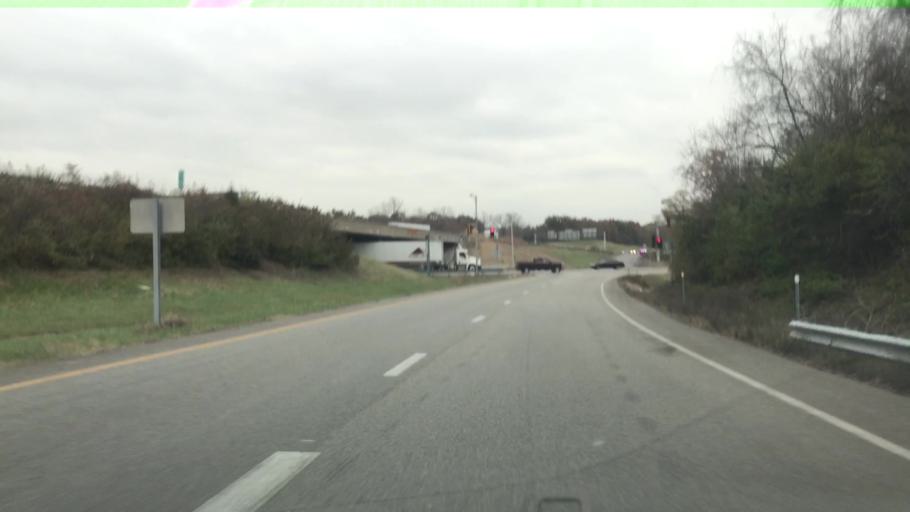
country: US
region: Missouri
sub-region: Clay County
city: Claycomo
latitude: 39.2033
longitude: -94.4935
